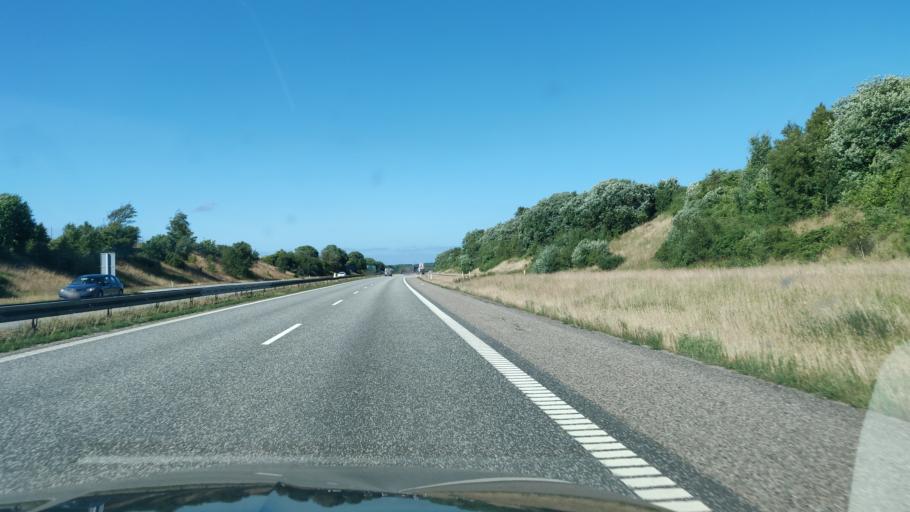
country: DK
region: North Denmark
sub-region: Mariagerfjord Kommune
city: Arden
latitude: 56.7846
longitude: 9.6984
